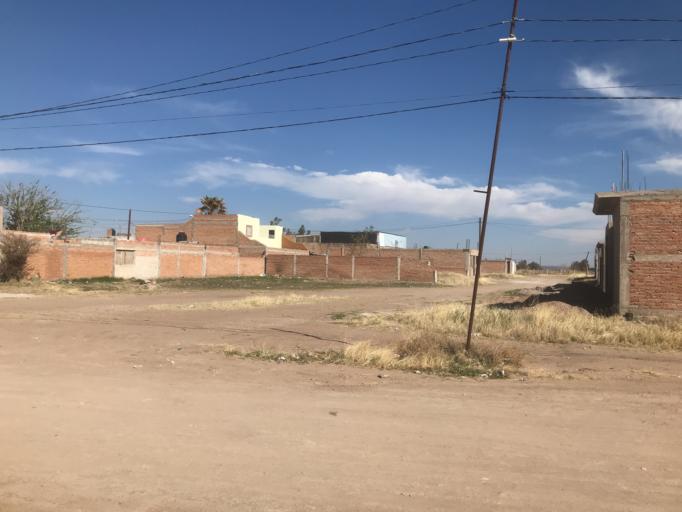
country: MX
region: Durango
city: Victoria de Durango
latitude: 24.0225
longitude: -104.5917
